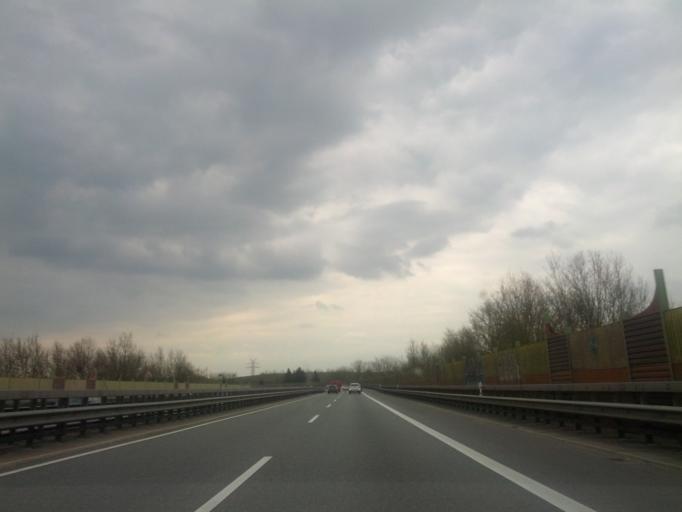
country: DE
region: Lower Saxony
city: Oldenburg
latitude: 53.1257
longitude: 8.2164
